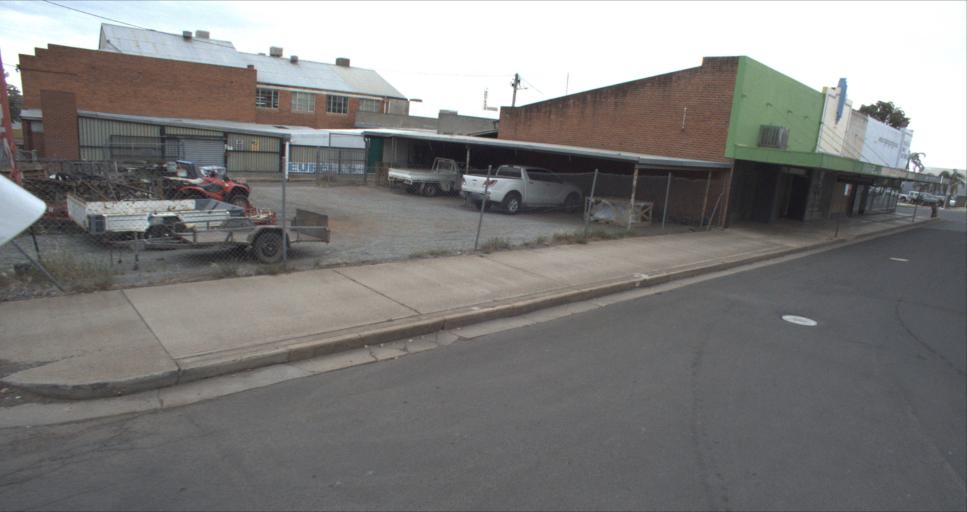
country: AU
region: New South Wales
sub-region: Leeton
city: Leeton
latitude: -34.5523
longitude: 146.4024
